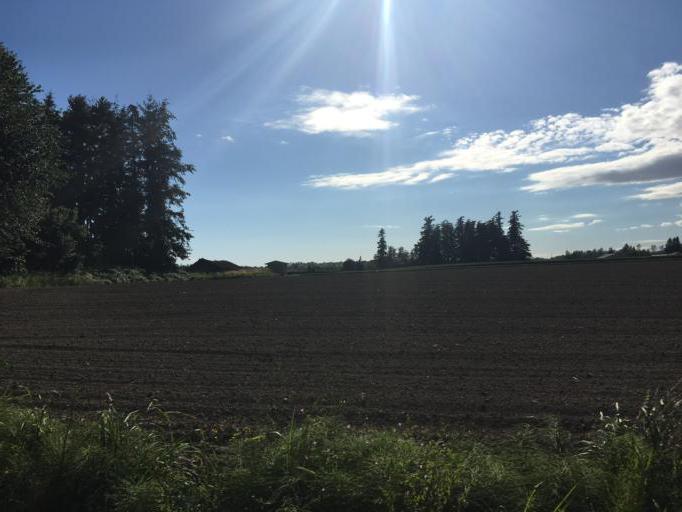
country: US
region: Washington
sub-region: Whatcom County
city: Nooksack
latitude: 48.8809
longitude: -122.3097
